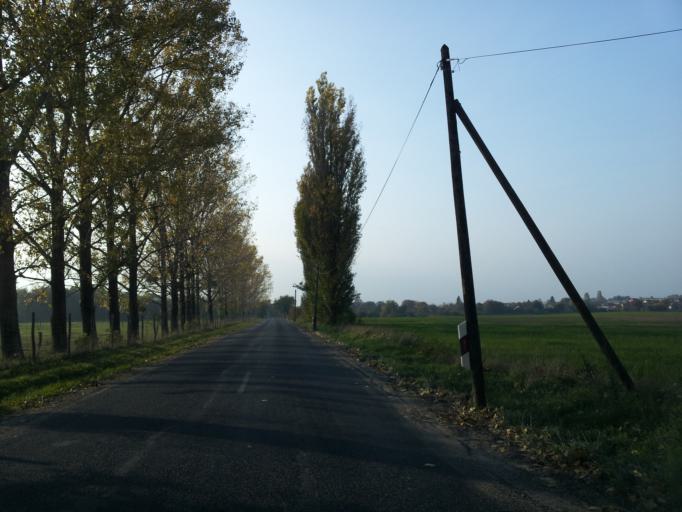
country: HU
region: Komarom-Esztergom
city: Kisber
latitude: 47.4908
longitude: 18.0438
